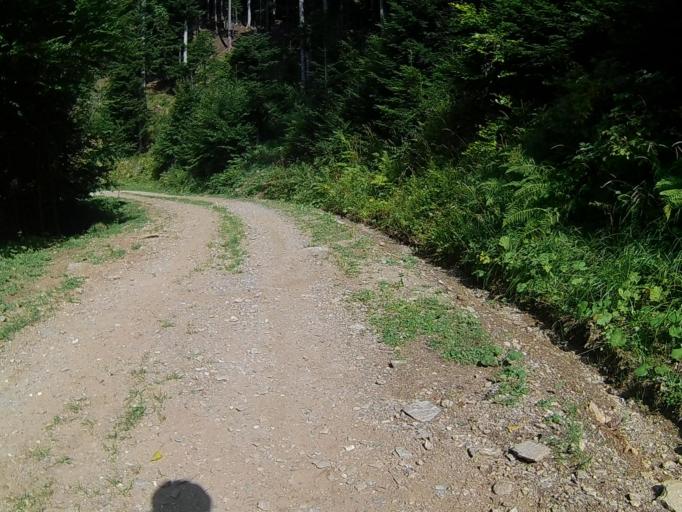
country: SI
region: Ruse
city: Ruse
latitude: 46.5050
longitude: 15.5366
